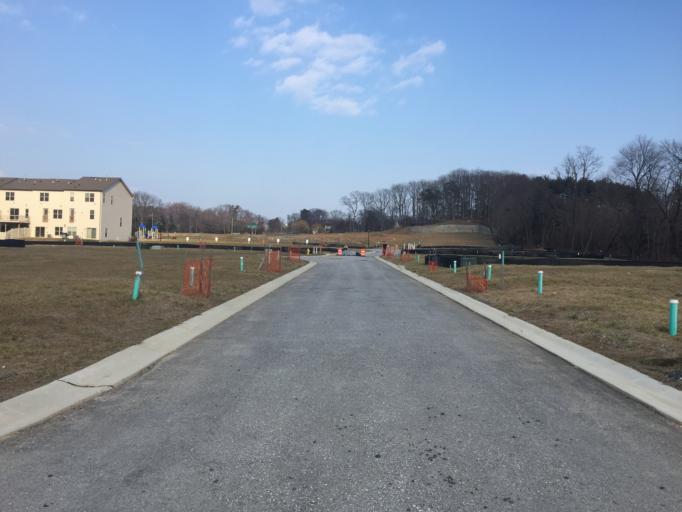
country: US
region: Maryland
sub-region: Anne Arundel County
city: South Gate
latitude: 39.1106
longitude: -76.6303
